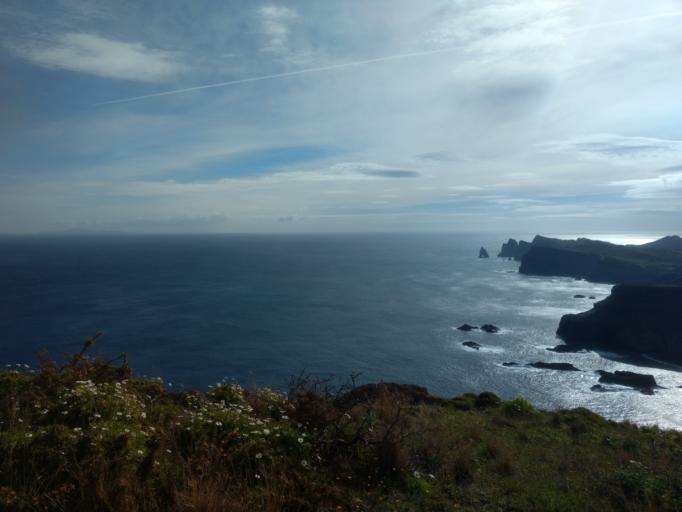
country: PT
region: Madeira
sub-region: Machico
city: Canical
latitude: 32.7526
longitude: -16.7421
